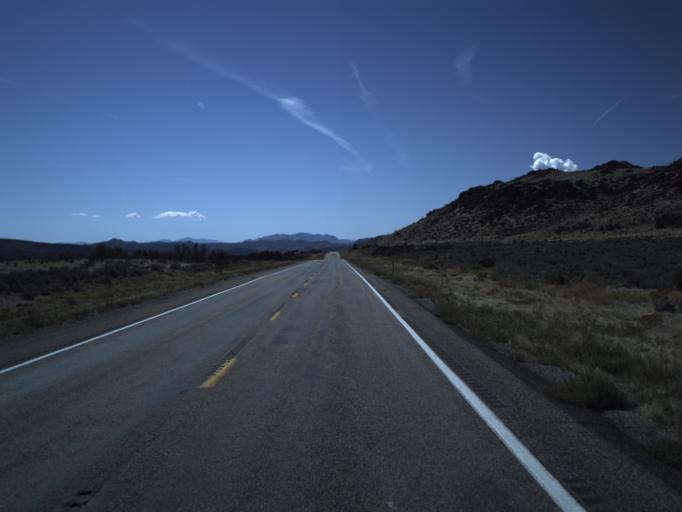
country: US
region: Utah
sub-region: Washington County
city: Enterprise
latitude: 37.3854
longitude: -113.6504
